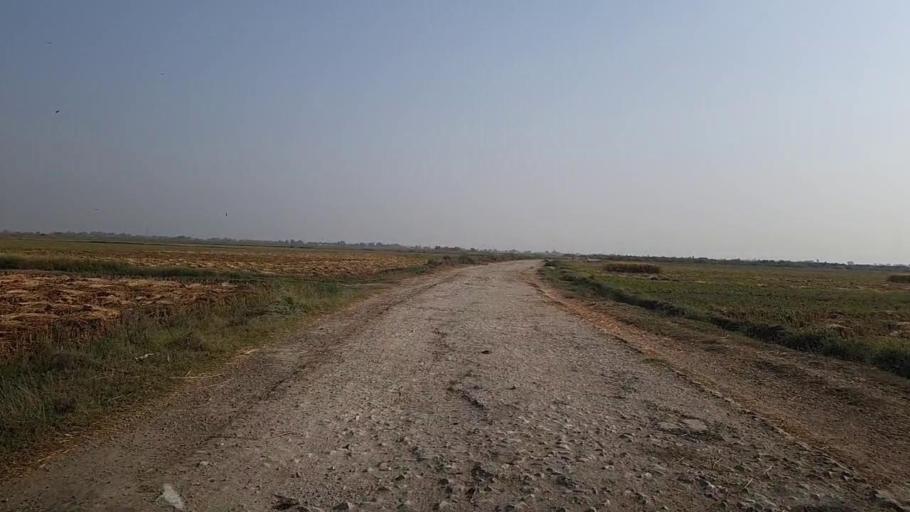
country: PK
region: Sindh
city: Kandhkot
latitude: 28.2984
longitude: 69.2520
